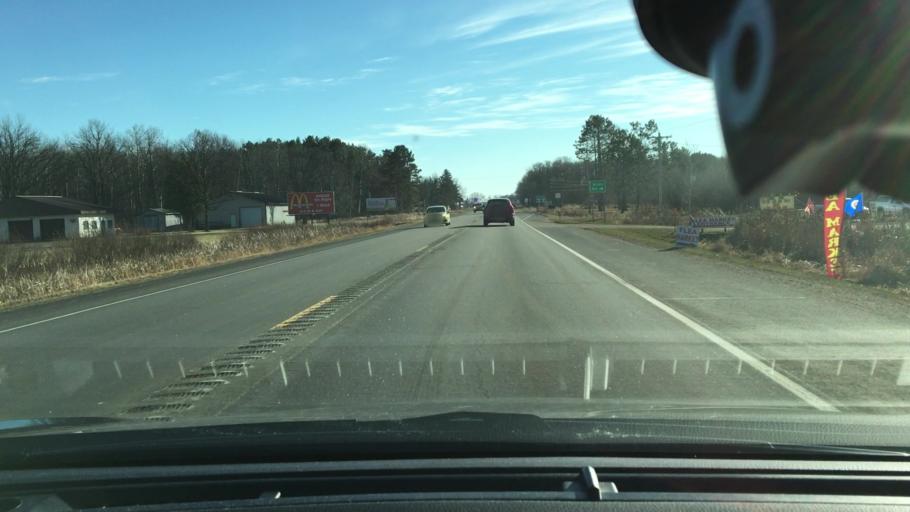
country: US
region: Minnesota
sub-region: Mille Lacs County
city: Vineland
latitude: 46.3030
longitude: -93.8293
